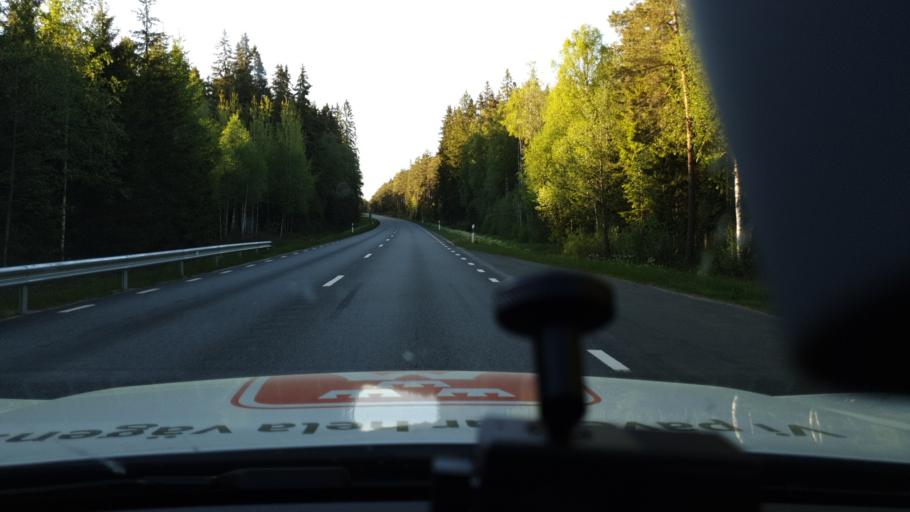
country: SE
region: Joenkoeping
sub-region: Vetlanda Kommun
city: Ekenassjon
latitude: 57.5781
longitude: 14.9716
